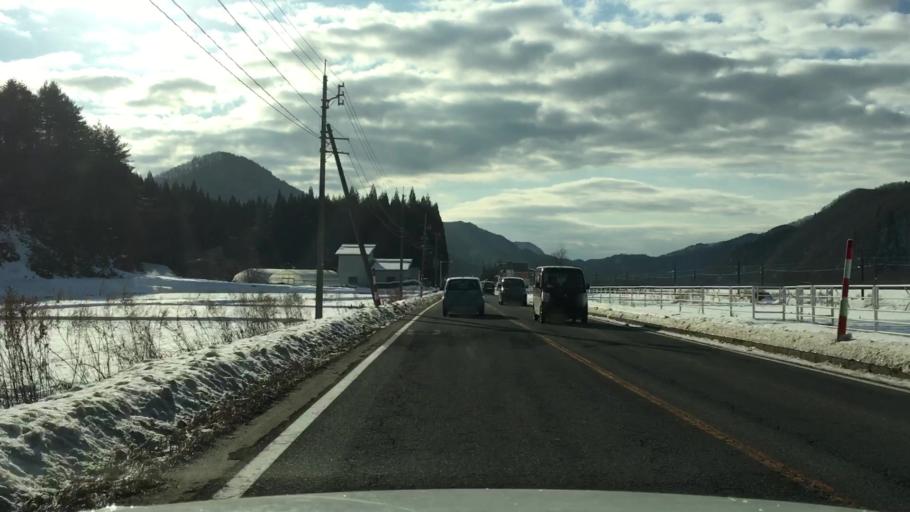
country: JP
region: Akita
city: Odate
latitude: 40.3599
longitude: 140.5974
